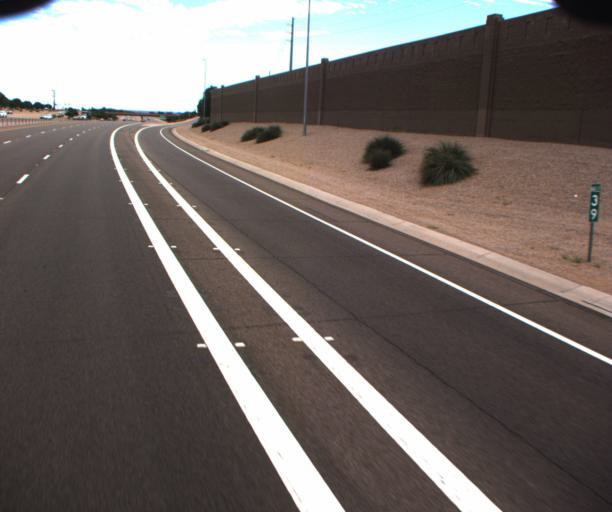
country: US
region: Arizona
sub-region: Maricopa County
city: Gilbert
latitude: 33.3276
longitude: -111.7278
